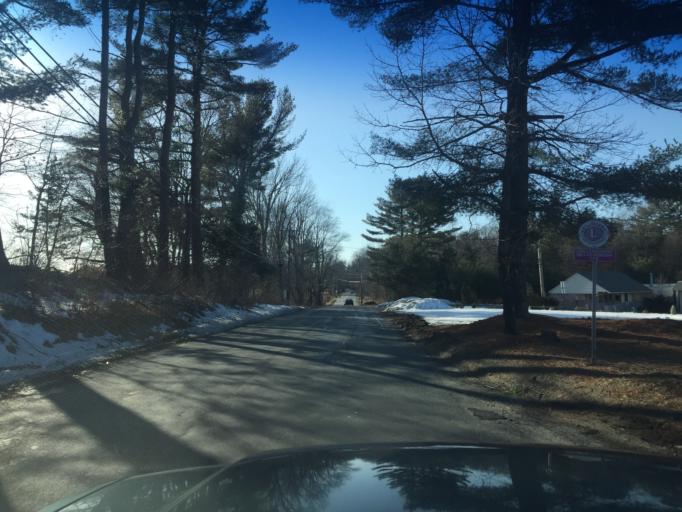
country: US
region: Massachusetts
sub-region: Norfolk County
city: Bellingham
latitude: 42.0886
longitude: -71.4984
